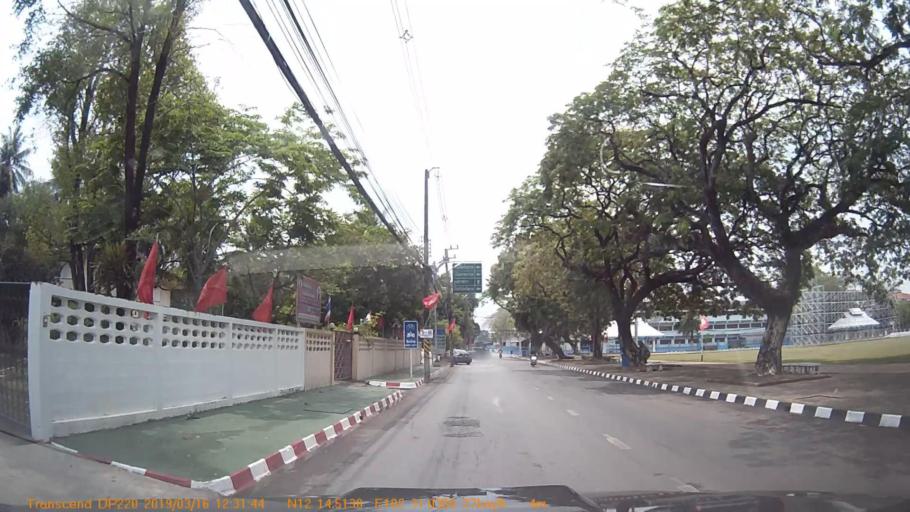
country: TH
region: Trat
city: Trat
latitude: 12.2418
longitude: 102.5171
